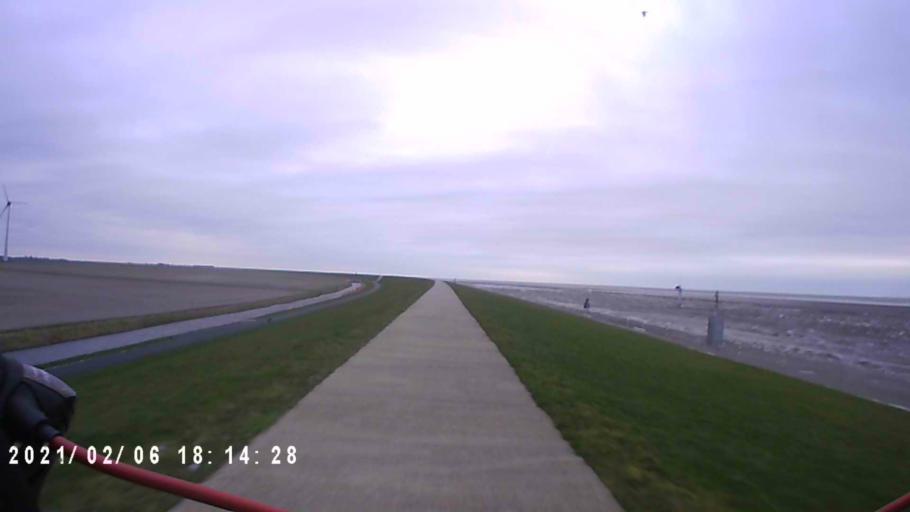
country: DE
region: Lower Saxony
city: Borkum
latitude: 53.4641
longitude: 6.7610
